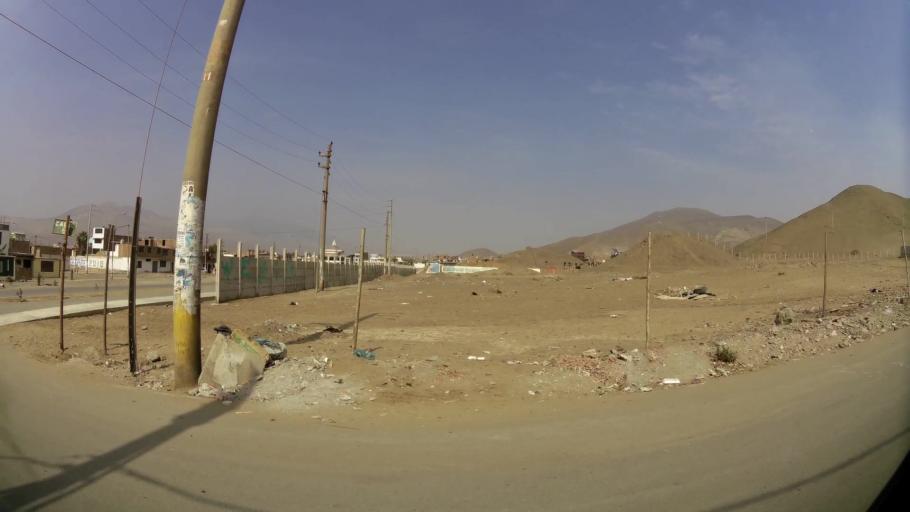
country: PE
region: Lima
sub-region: Lima
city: Santa Rosa
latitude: -11.7855
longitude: -77.1592
